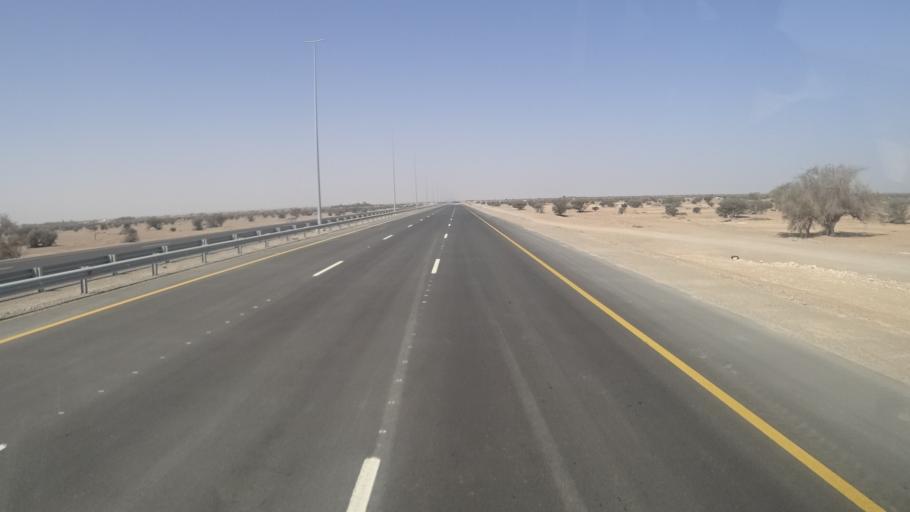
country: OM
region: Ash Sharqiyah
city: Sur
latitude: 22.2723
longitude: 59.2404
